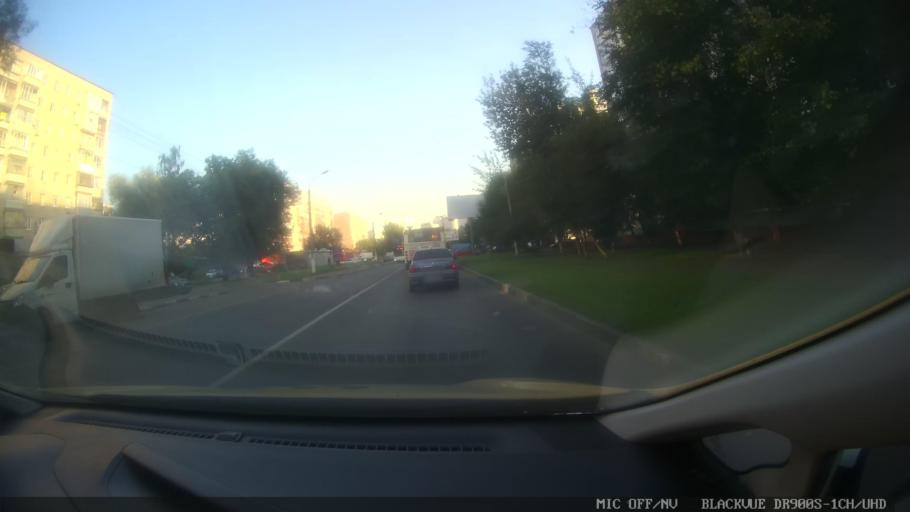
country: RU
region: Moscow
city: Nekrasovka
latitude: 55.6973
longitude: 37.9000
